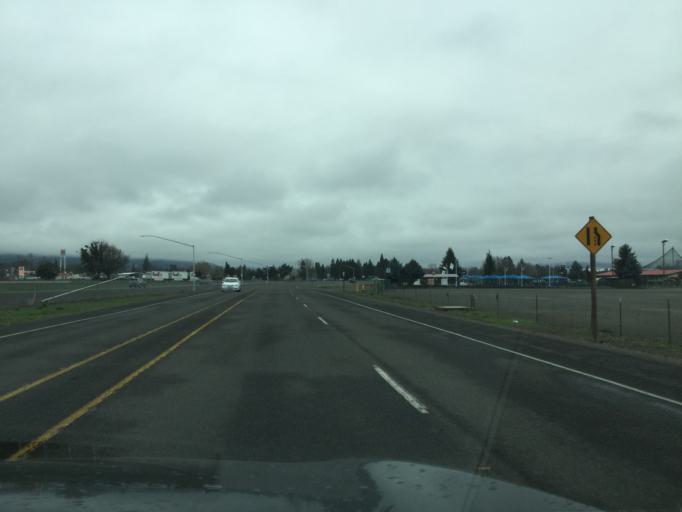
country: US
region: Oregon
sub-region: Jackson County
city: Central Point
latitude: 42.3796
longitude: -122.9021
